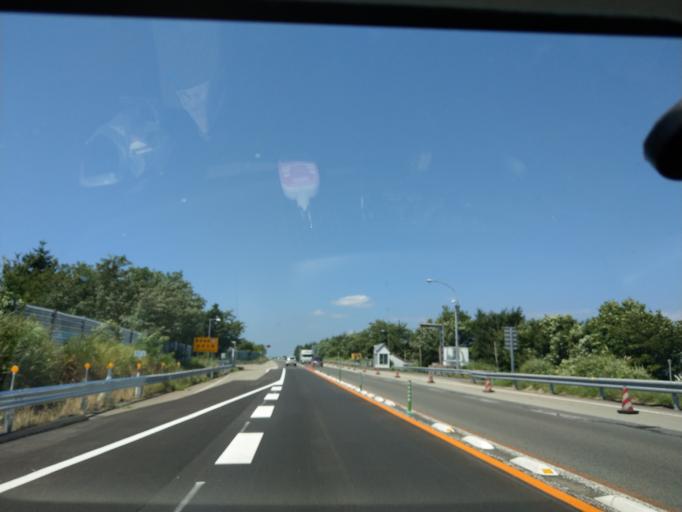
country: JP
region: Akita
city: Yokotemachi
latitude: 39.3293
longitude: 140.5099
